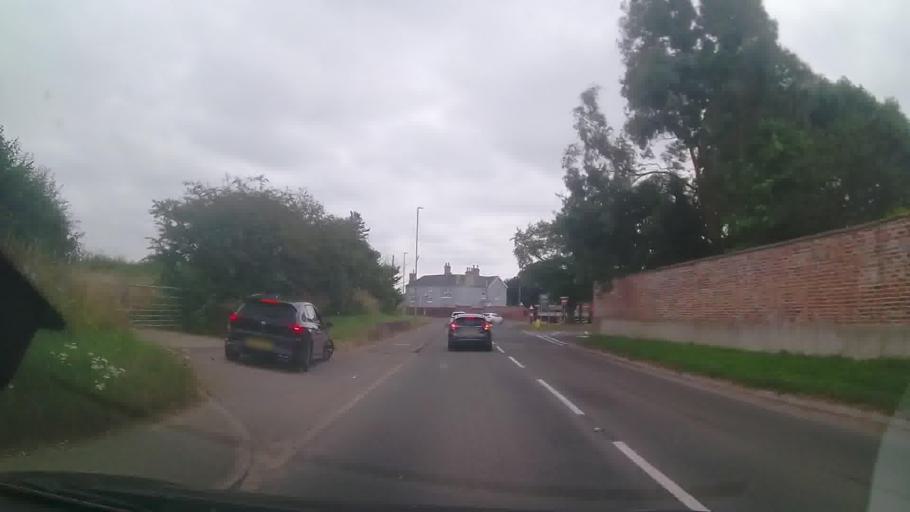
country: GB
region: England
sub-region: Leicestershire
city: Desford
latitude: 52.6348
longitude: -1.2785
